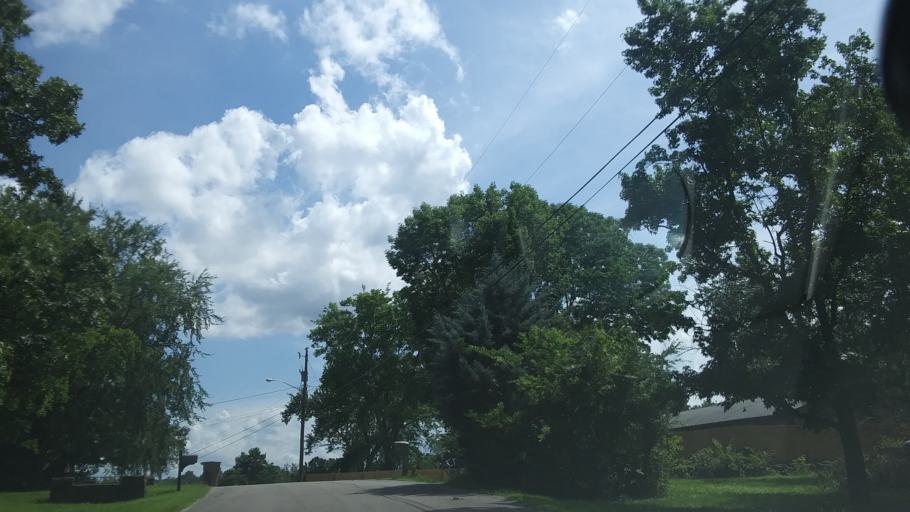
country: US
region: Tennessee
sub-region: Rutherford County
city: La Vergne
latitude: 36.0774
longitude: -86.6373
